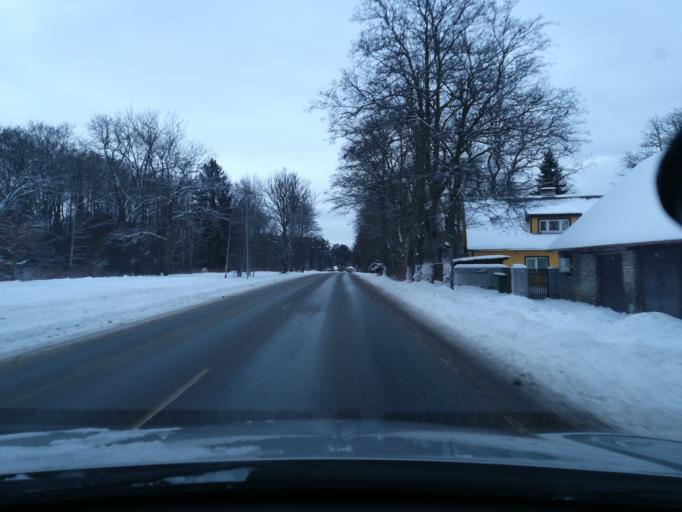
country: EE
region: Harju
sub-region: Keila linn
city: Keila
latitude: 59.4365
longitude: 24.3698
